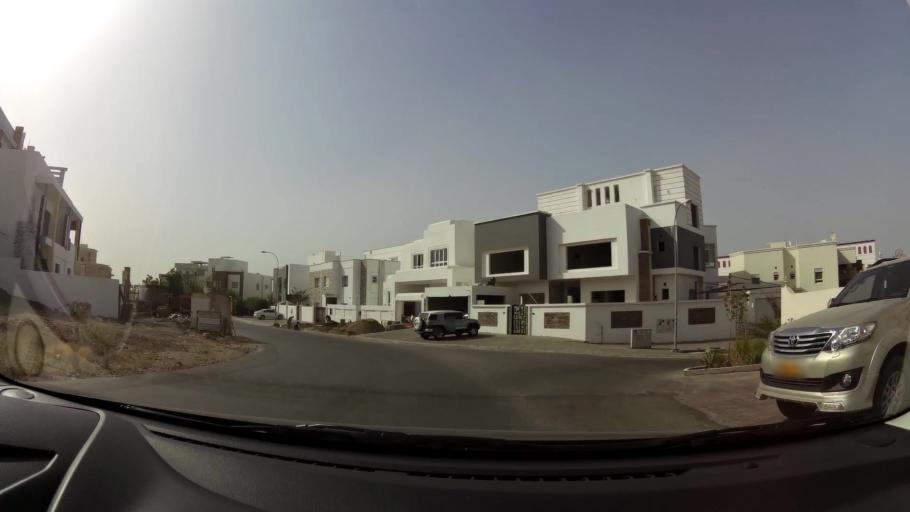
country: OM
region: Muhafazat Masqat
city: Bawshar
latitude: 23.5619
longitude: 58.3639
